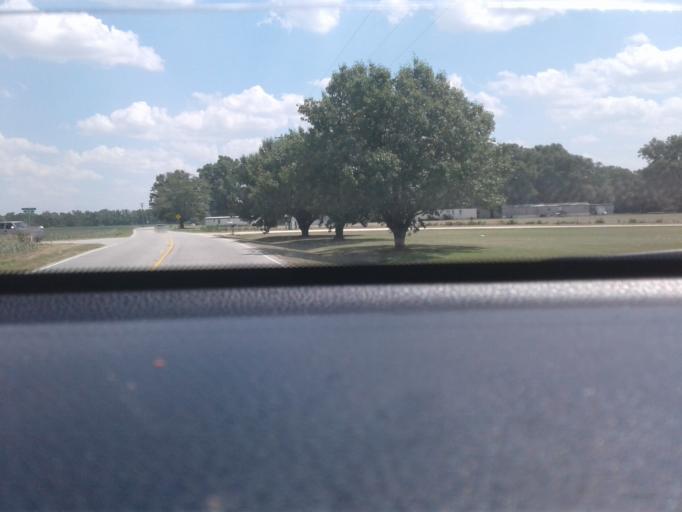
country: US
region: North Carolina
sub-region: Harnett County
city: Erwin
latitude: 35.2966
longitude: -78.6664
